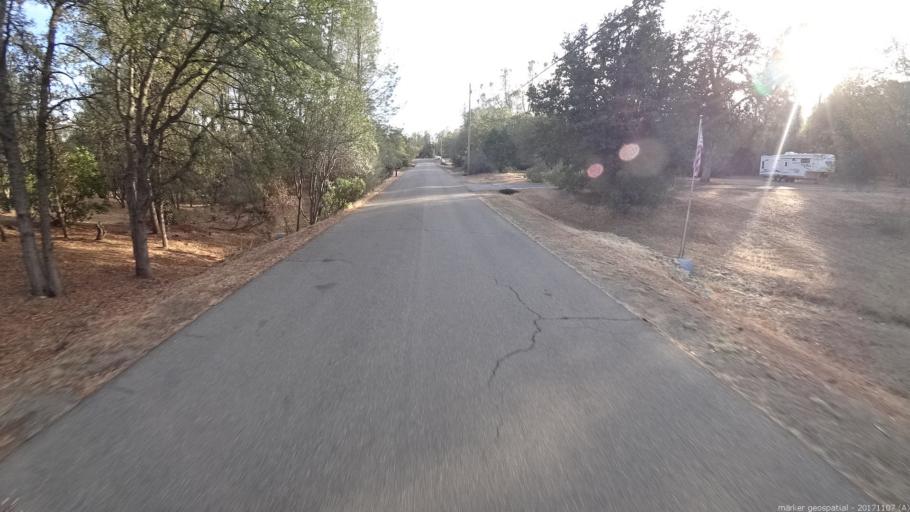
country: US
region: California
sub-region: Shasta County
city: Shasta
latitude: 40.5290
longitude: -122.4826
